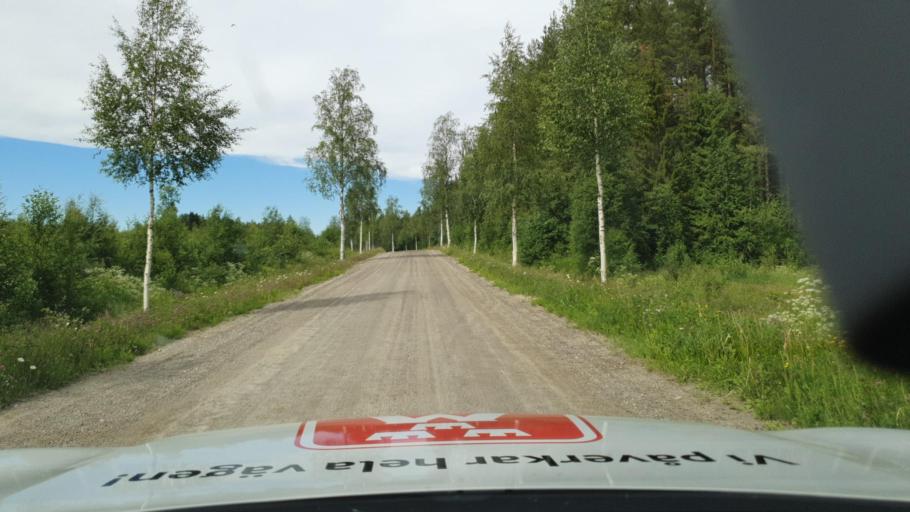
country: SE
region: Vaesterbotten
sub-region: Skelleftea Kommun
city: Burtraesk
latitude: 64.4672
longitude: 20.4611
